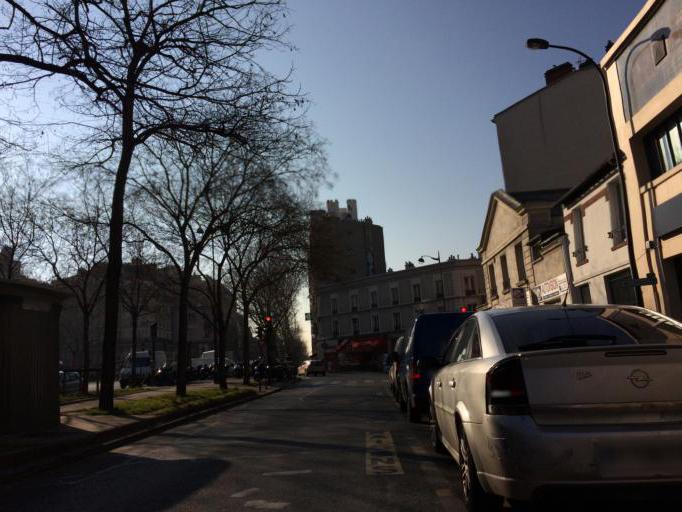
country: FR
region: Ile-de-France
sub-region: Departement de Seine-Saint-Denis
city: Bagnolet
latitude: 48.8590
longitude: 2.3892
